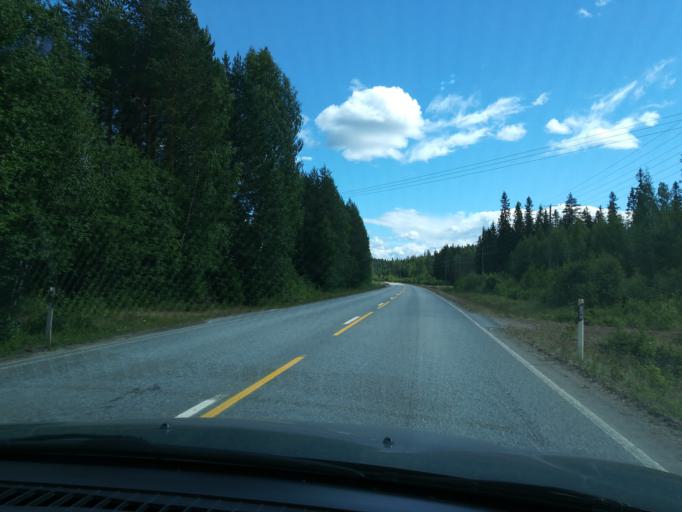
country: FI
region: Southern Savonia
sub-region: Mikkeli
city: Hirvensalmi
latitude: 61.6666
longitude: 26.9071
